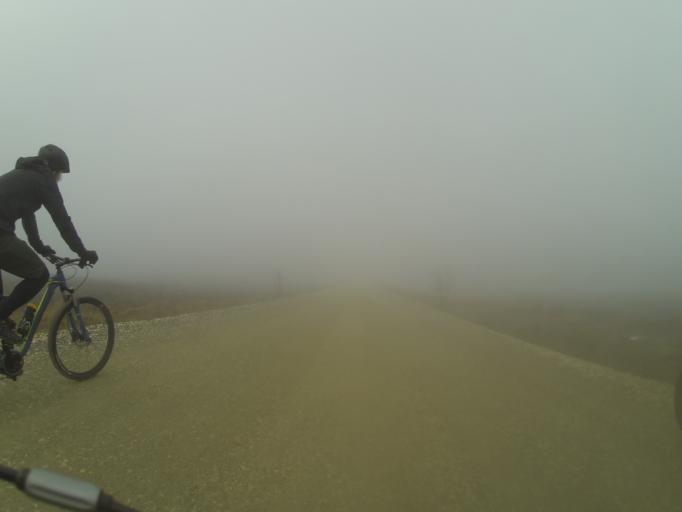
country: RO
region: Mehedinti
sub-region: Comuna Baclesu
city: Baclesu
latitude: 44.4475
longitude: 23.1267
